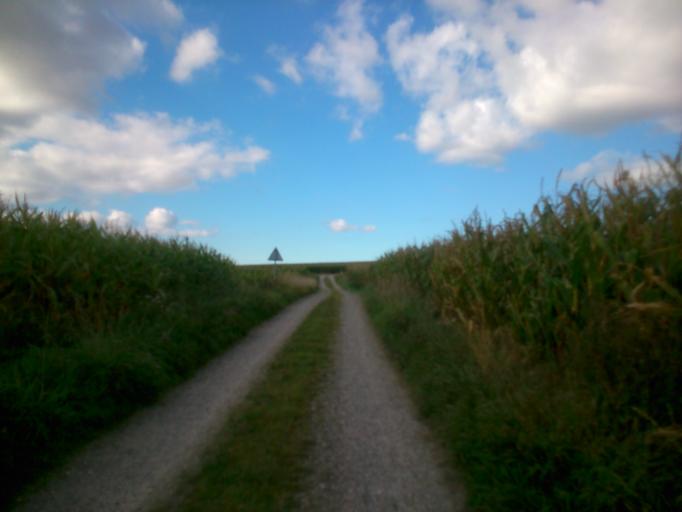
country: DK
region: North Denmark
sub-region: Thisted Kommune
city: Thisted
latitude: 56.9458
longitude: 8.5825
